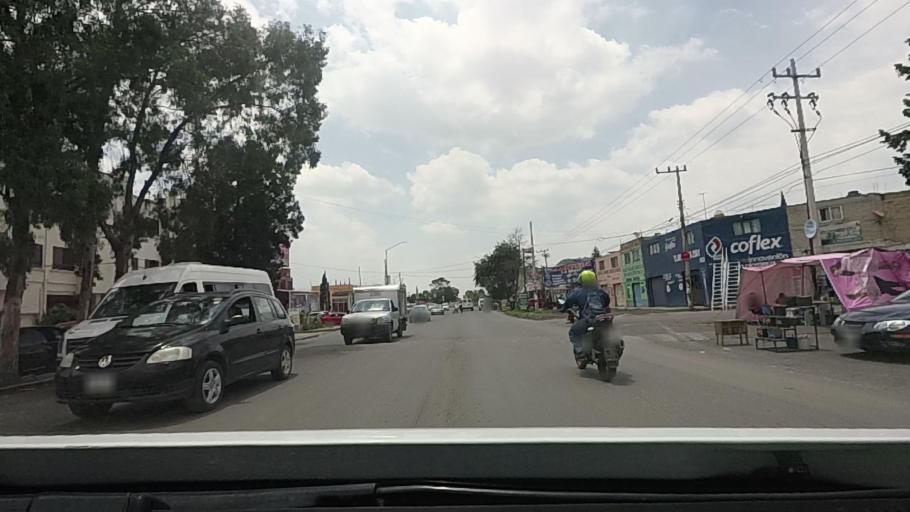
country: MX
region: Mexico
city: Chalco de Diaz Covarrubias
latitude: 19.2753
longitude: -98.9070
